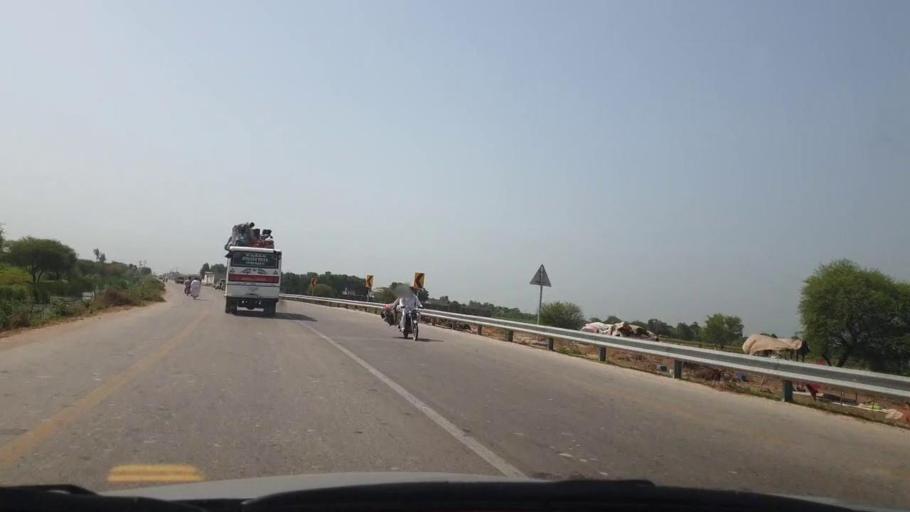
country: PK
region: Sindh
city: Matli
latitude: 25.0311
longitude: 68.6537
